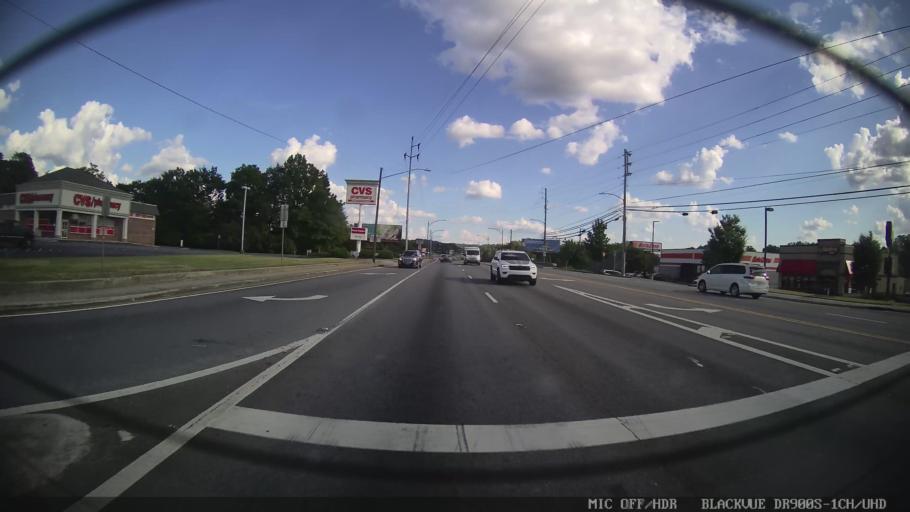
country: US
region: Georgia
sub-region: Floyd County
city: Rome
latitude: 34.2561
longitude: -85.1644
